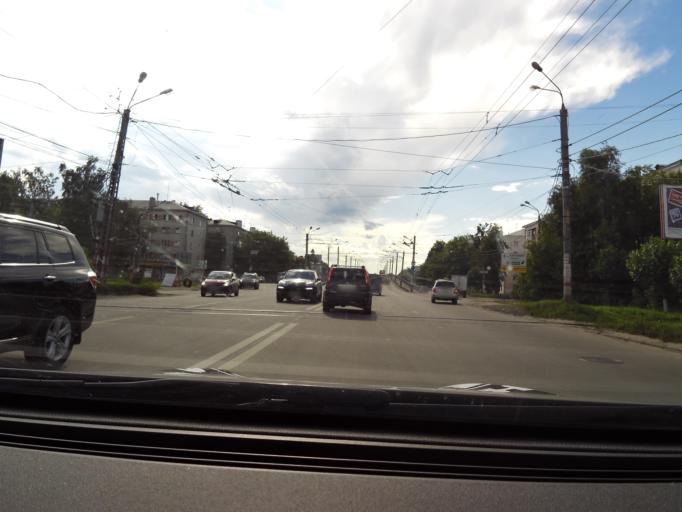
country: RU
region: Nizjnij Novgorod
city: Nizhniy Novgorod
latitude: 56.3150
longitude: 43.9041
